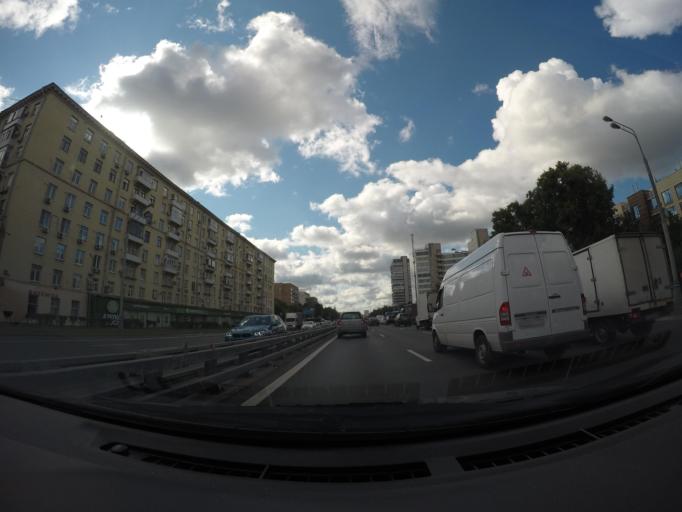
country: RU
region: Moskovskaya
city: Levoberezhnyy
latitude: 55.8341
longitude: 37.4854
